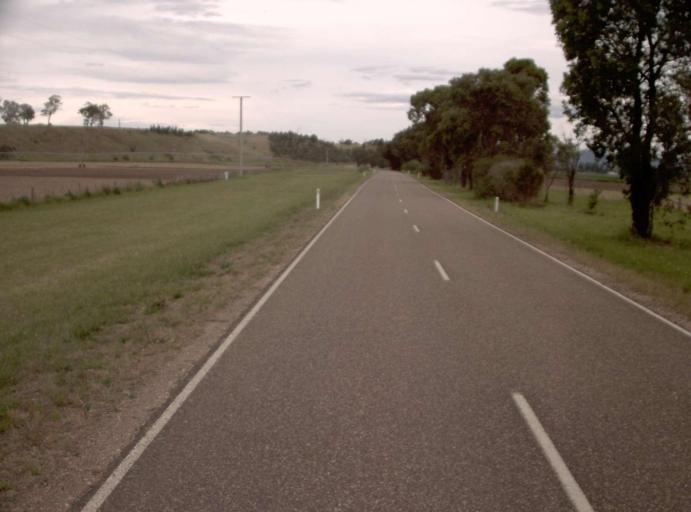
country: AU
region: Victoria
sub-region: East Gippsland
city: Bairnsdale
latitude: -37.7956
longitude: 147.4196
